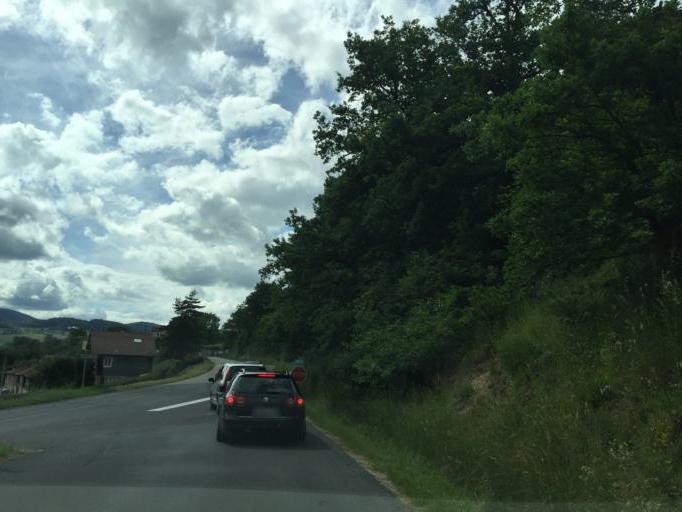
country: FR
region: Auvergne
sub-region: Departement du Puy-de-Dome
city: Ambert
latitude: 45.5436
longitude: 3.7577
